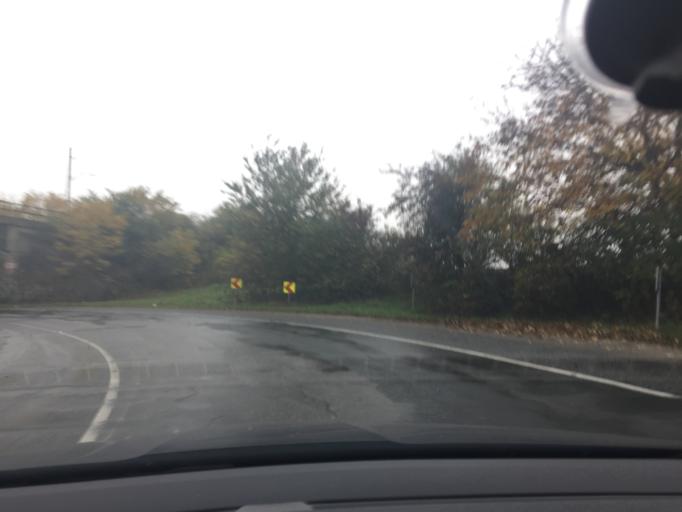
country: CZ
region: South Moravian
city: Rousinov
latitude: 49.1954
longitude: 16.8613
